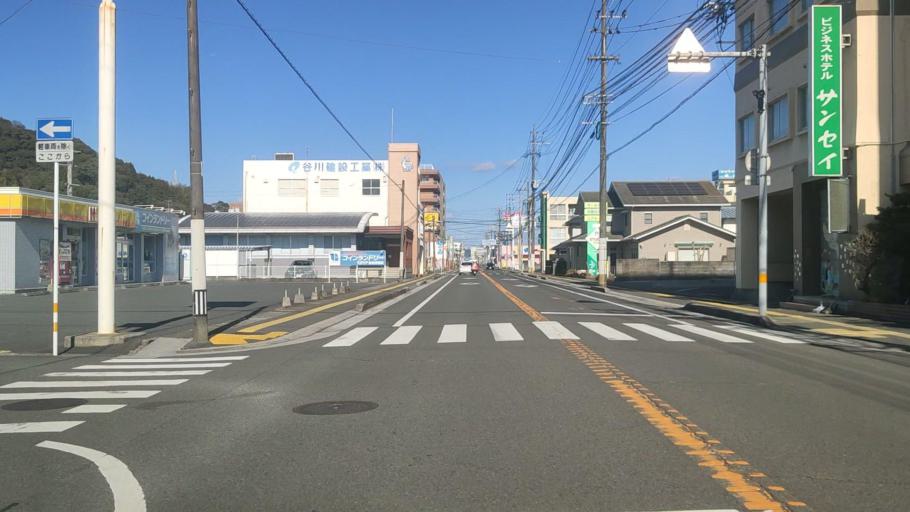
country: JP
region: Oita
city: Saiki
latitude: 32.9628
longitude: 131.9022
